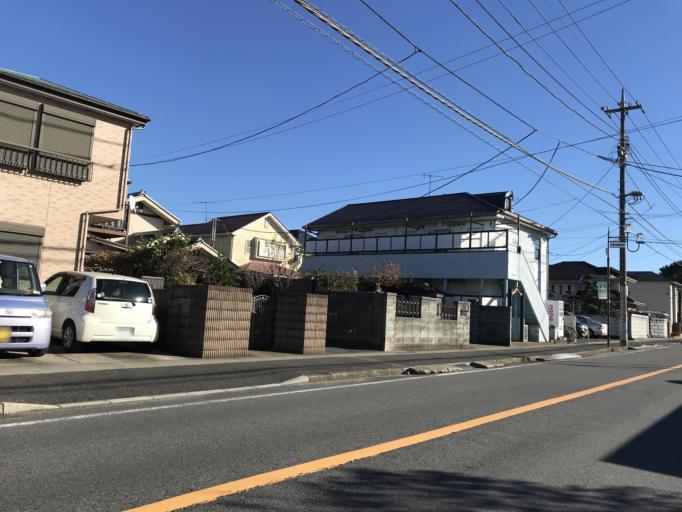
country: JP
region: Chiba
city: Nagareyama
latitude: 35.8271
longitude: 139.9323
